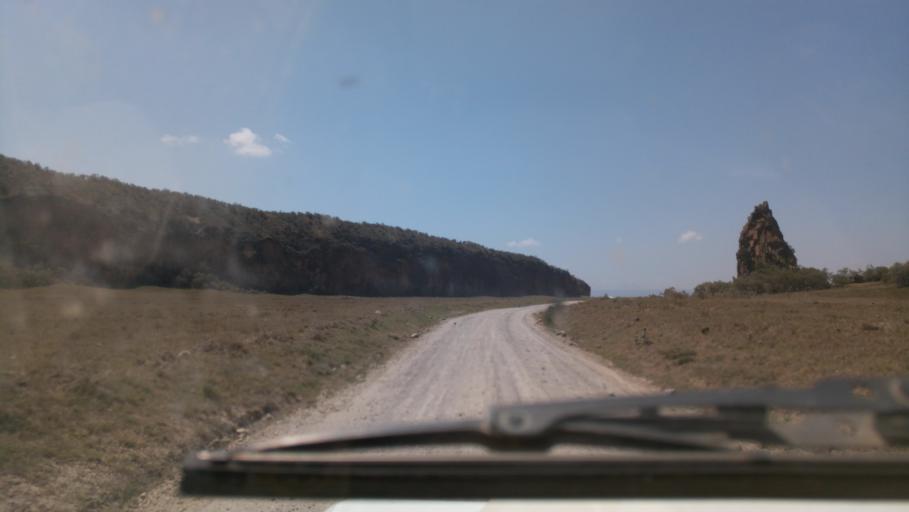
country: KE
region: Nakuru
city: Naivasha
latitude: -0.8605
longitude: 36.3597
